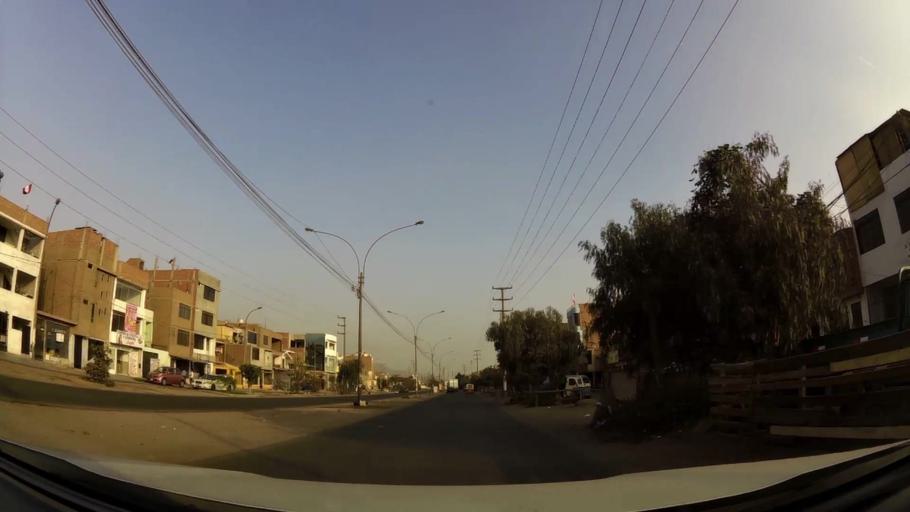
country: PE
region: Lima
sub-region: Lima
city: Independencia
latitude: -11.9531
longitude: -77.0647
